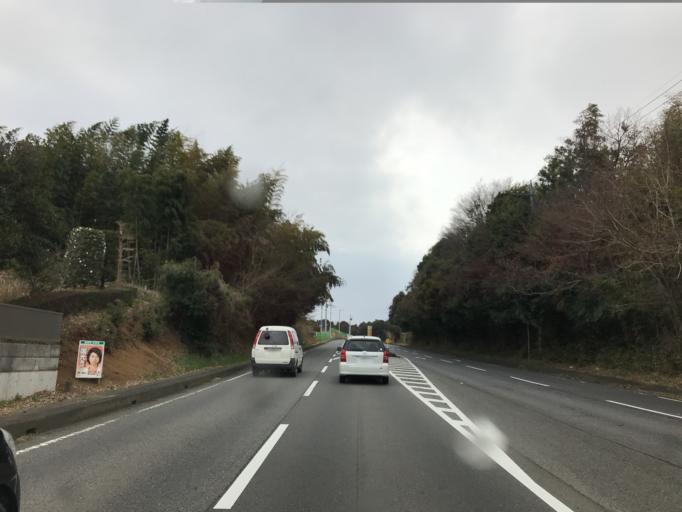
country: JP
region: Ibaraki
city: Ushiku
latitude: 35.9993
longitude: 140.0759
